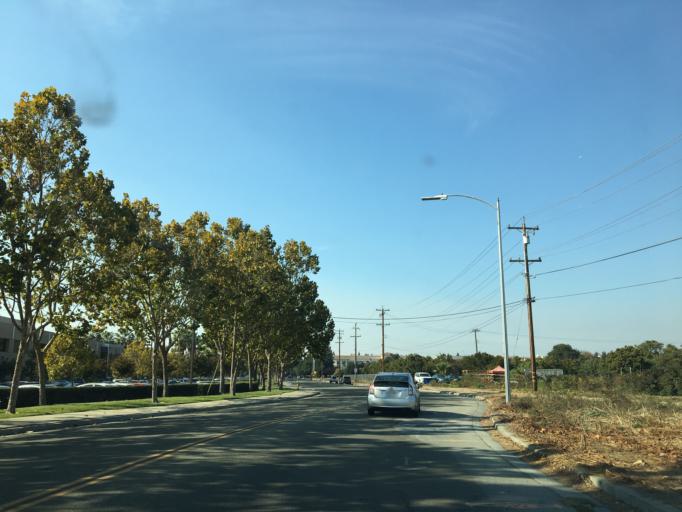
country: US
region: California
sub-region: Santa Clara County
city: Milpitas
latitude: 37.3953
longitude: -121.9172
